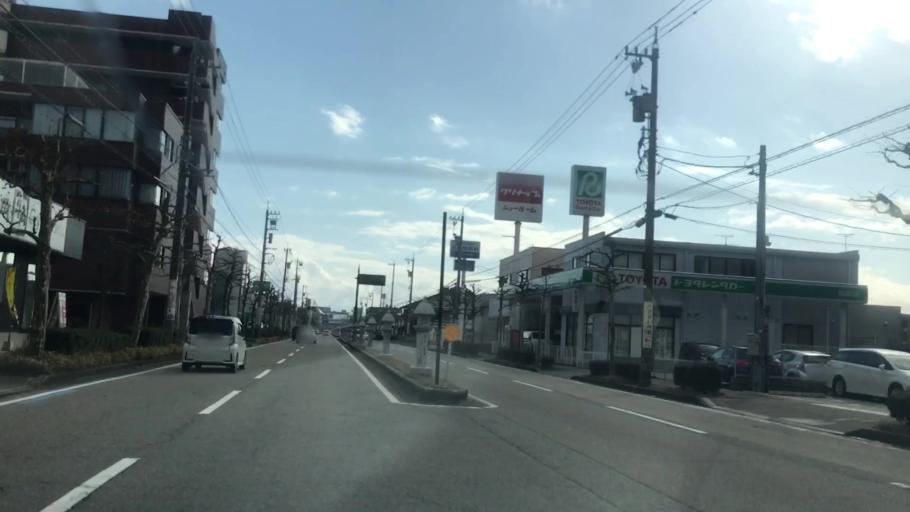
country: JP
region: Toyama
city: Takaoka
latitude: 36.7339
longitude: 137.0155
